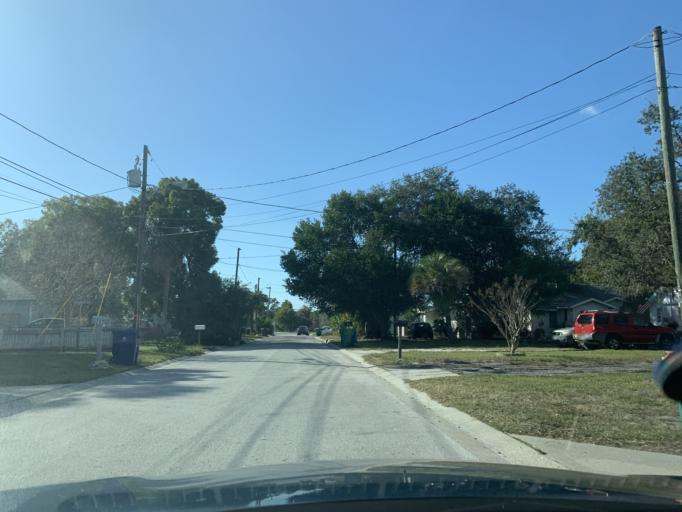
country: US
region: Florida
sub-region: Pinellas County
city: Belleair
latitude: 27.9342
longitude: -82.7944
